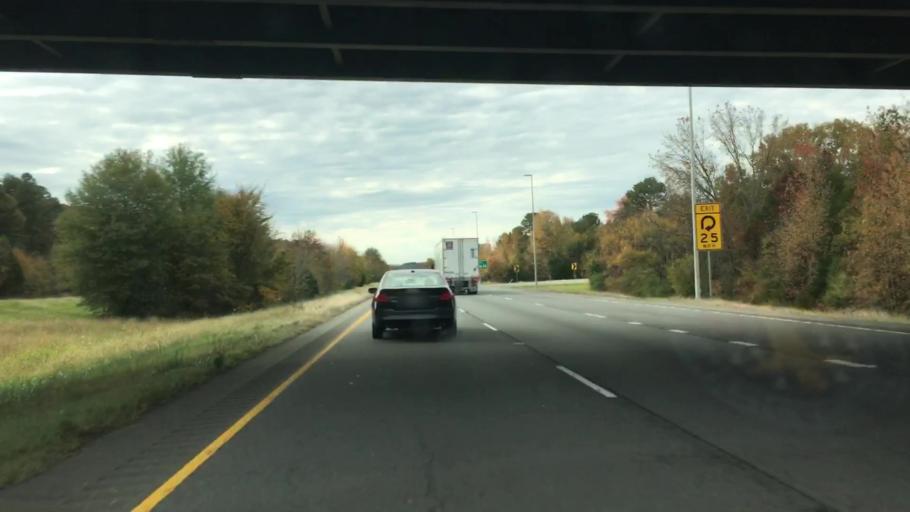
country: US
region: Arkansas
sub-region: Faulkner County
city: Conway
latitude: 35.1192
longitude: -92.4601
